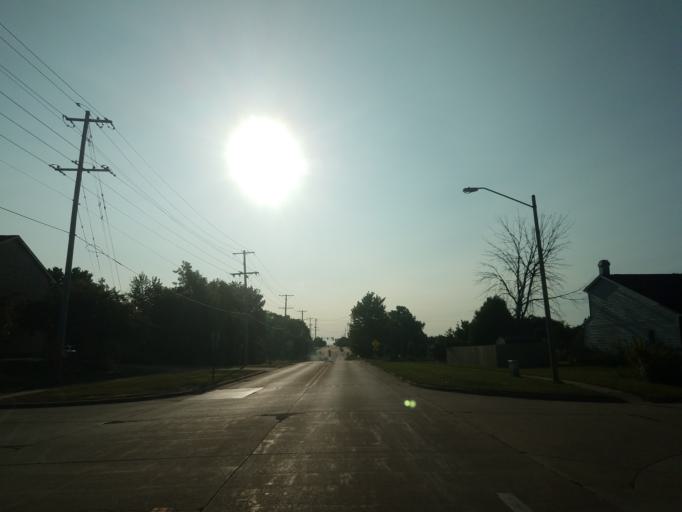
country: US
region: Illinois
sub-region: McLean County
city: Normal
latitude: 40.5316
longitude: -88.9870
